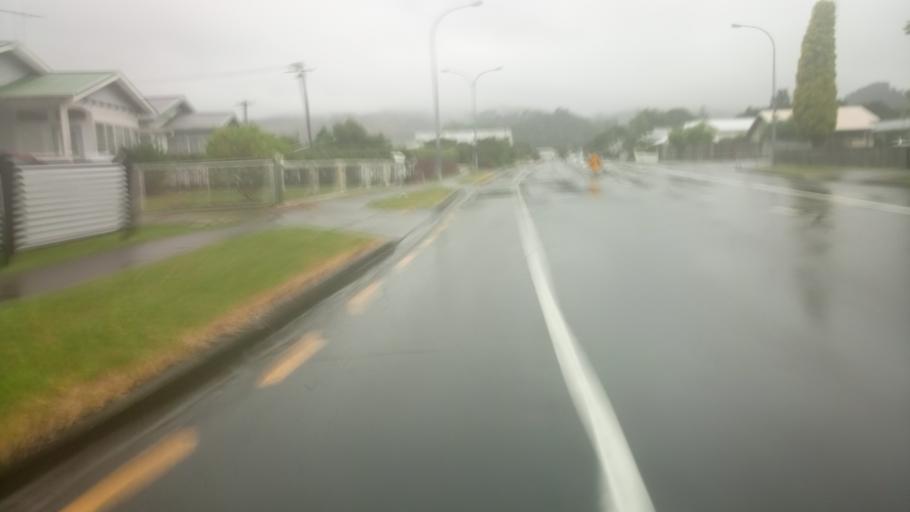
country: NZ
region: Gisborne
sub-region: Gisborne District
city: Gisborne
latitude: -38.6578
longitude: 178.0162
